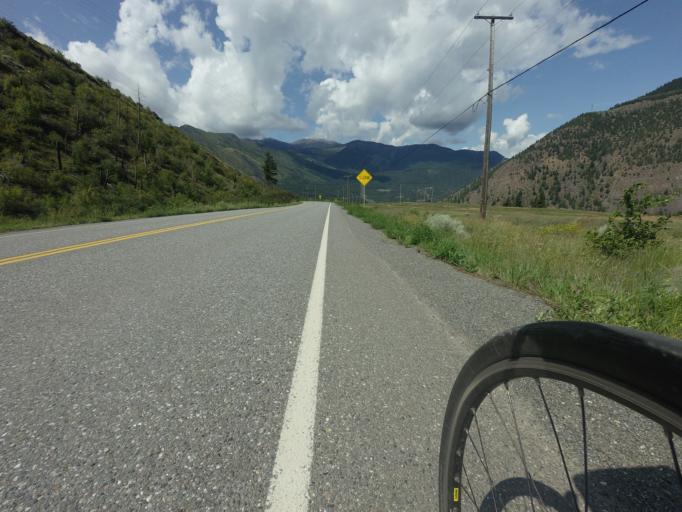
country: CA
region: British Columbia
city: Lillooet
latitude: 50.7564
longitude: -121.9193
